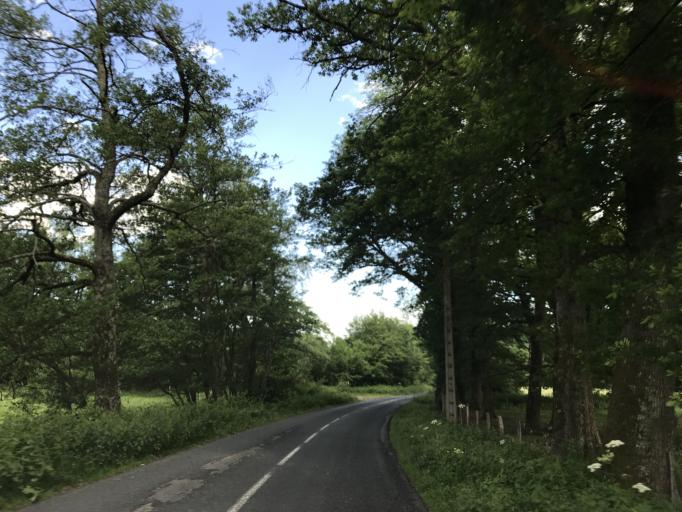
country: FR
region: Auvergne
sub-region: Departement du Puy-de-Dome
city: Courpiere
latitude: 45.7702
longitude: 3.6001
